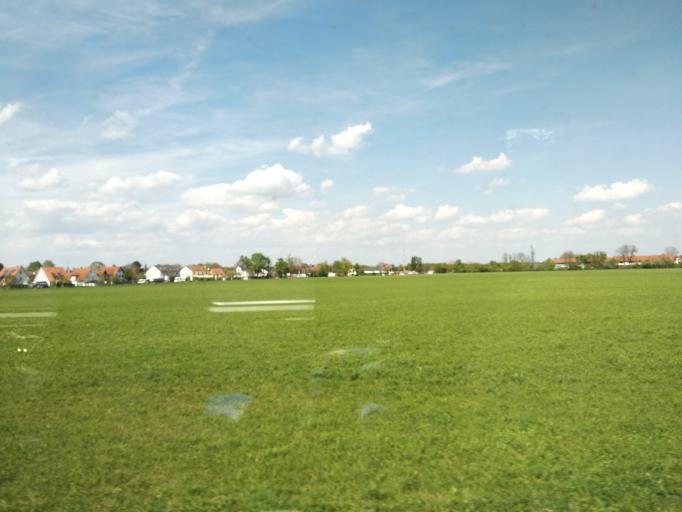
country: DE
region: Bavaria
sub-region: Upper Bavaria
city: Haar
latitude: 48.1179
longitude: 11.7016
